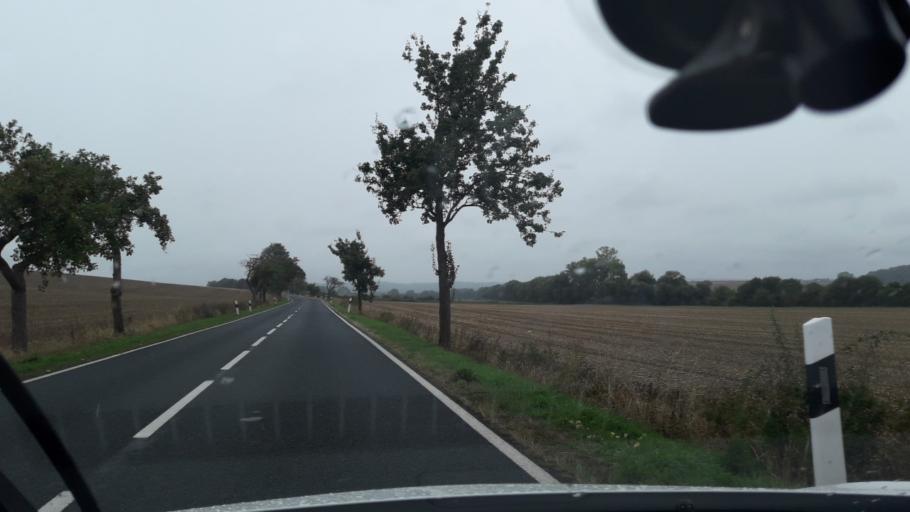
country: DE
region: Lower Saxony
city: Schladen
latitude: 52.0042
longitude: 10.5390
